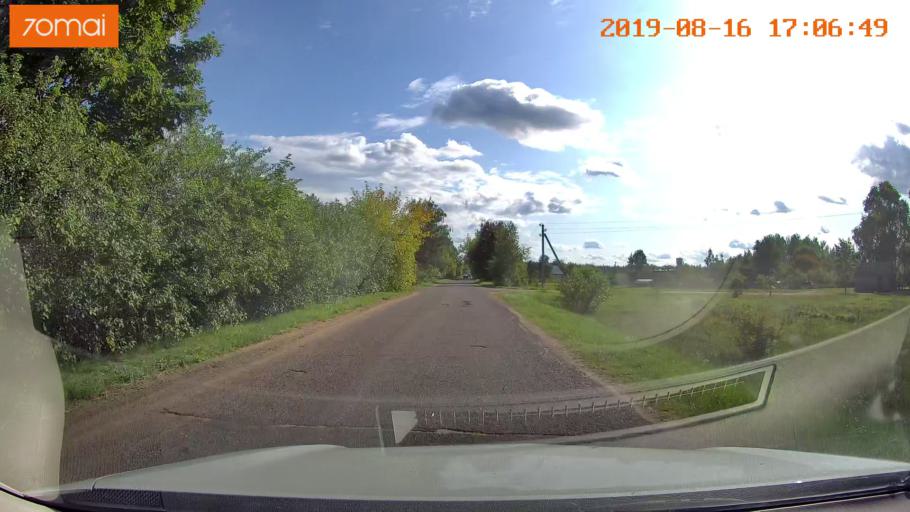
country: BY
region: Mogilev
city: Hlusha
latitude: 53.2229
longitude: 28.9288
